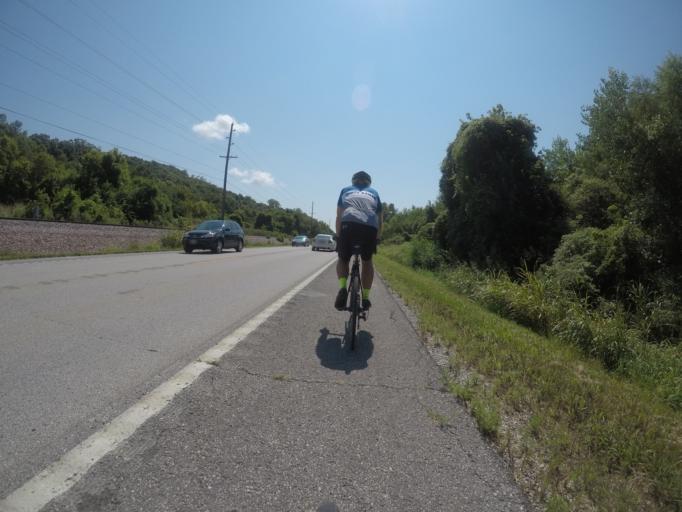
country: US
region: Missouri
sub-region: Platte County
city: Weston
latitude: 39.4714
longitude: -94.9816
